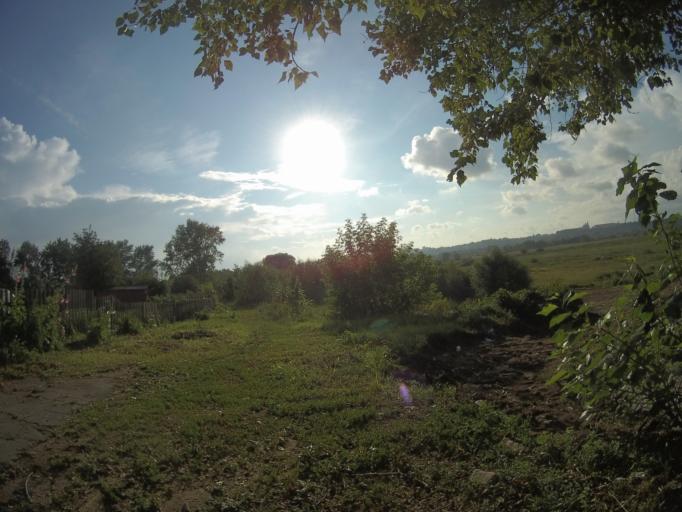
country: RU
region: Vladimir
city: Kommunar
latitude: 56.1121
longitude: 40.4324
